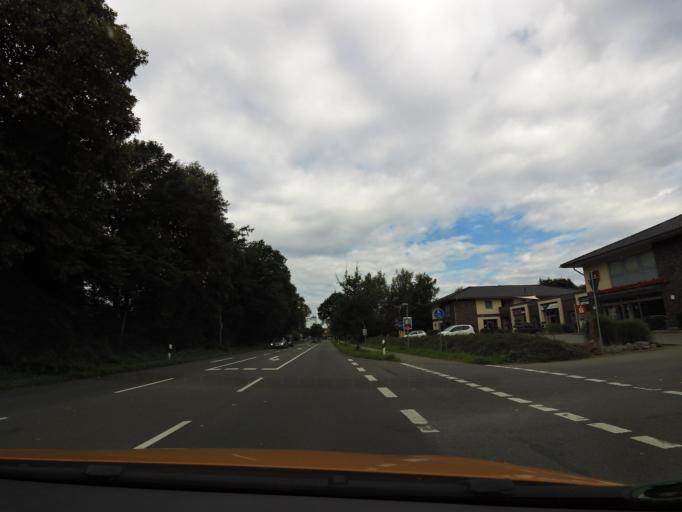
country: DE
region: Lower Saxony
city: Oldenburg
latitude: 53.1668
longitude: 8.1552
